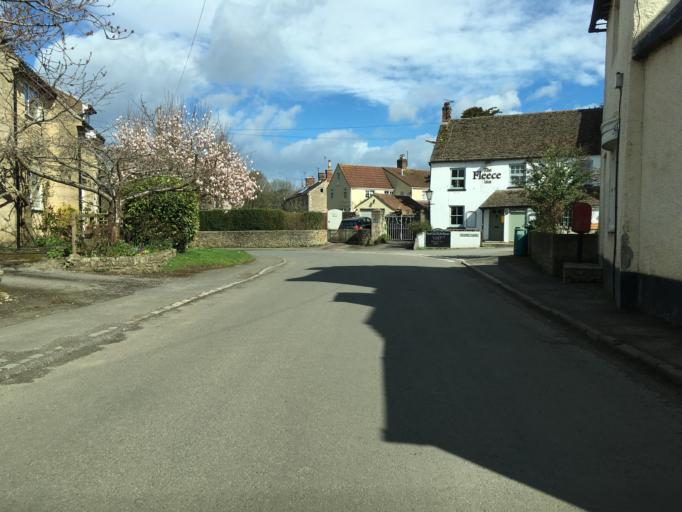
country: GB
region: England
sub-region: Gloucestershire
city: Wotton-under-Edge
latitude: 51.6051
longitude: -2.3346
